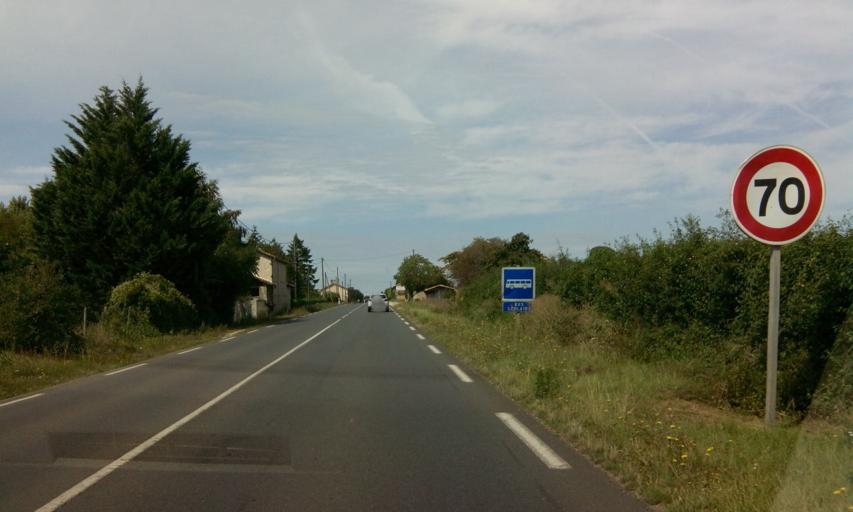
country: FR
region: Poitou-Charentes
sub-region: Departement des Deux-Sevres
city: Sauze-Vaussais
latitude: 46.1364
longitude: 0.1558
